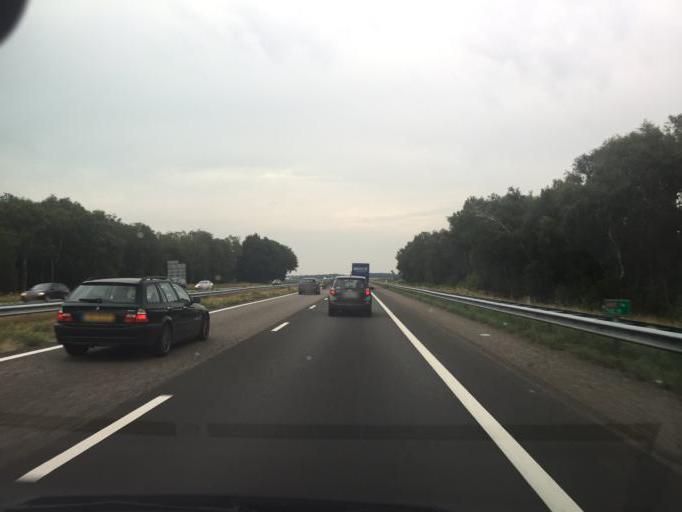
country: NL
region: North Brabant
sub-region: Gemeente Asten
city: Asten
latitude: 51.3869
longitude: 5.8796
